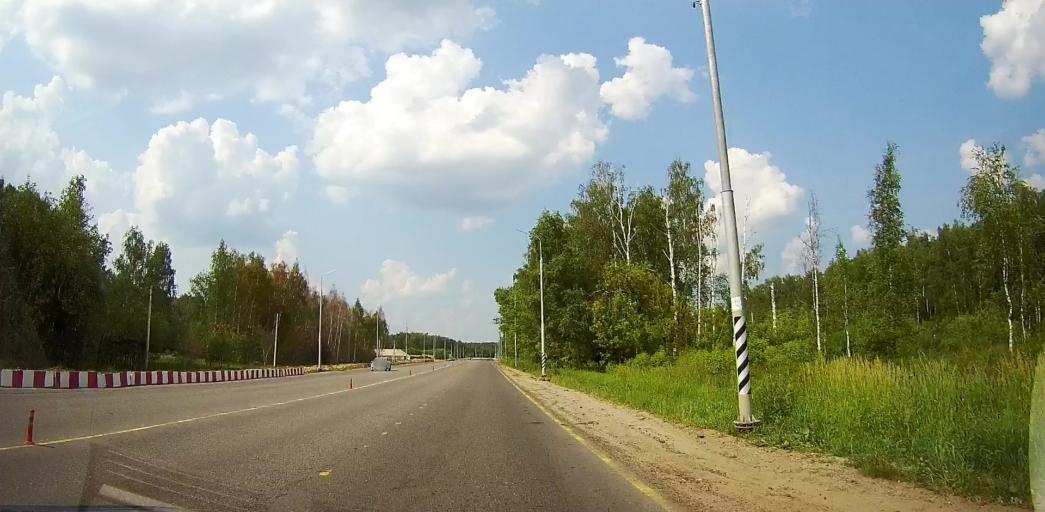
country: RU
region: Moskovskaya
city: Mikhnevo
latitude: 55.0691
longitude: 37.9526
